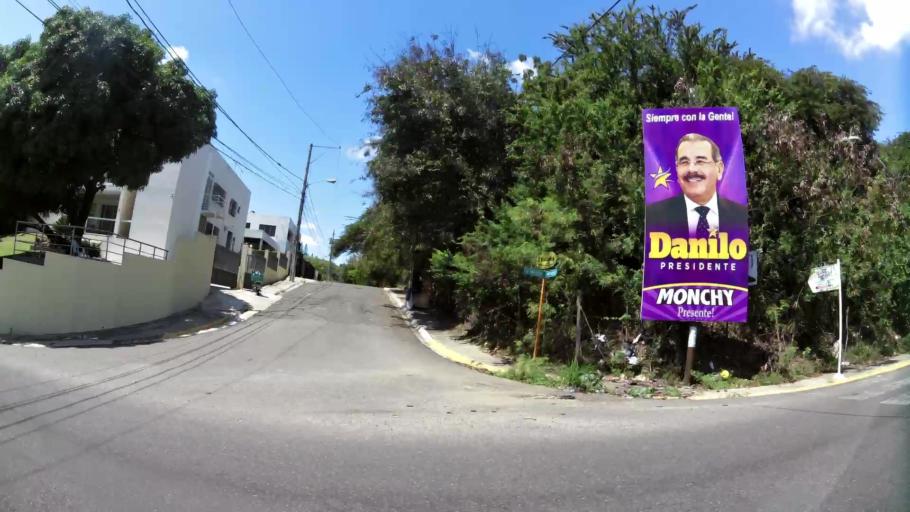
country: DO
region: Santiago
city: Santiago de los Caballeros
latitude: 19.4645
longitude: -70.6807
